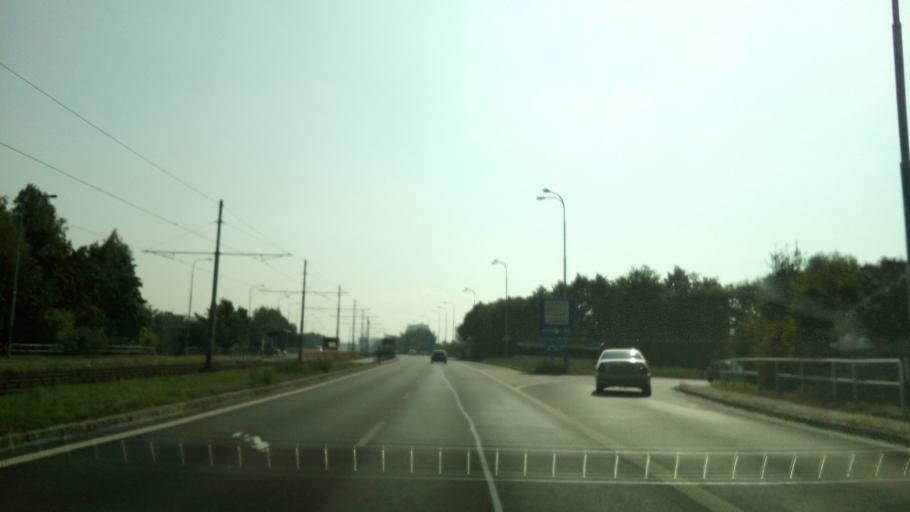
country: CZ
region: Moravskoslezsky
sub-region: Okres Ostrava-Mesto
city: Ostrava
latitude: 49.8065
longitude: 18.2443
